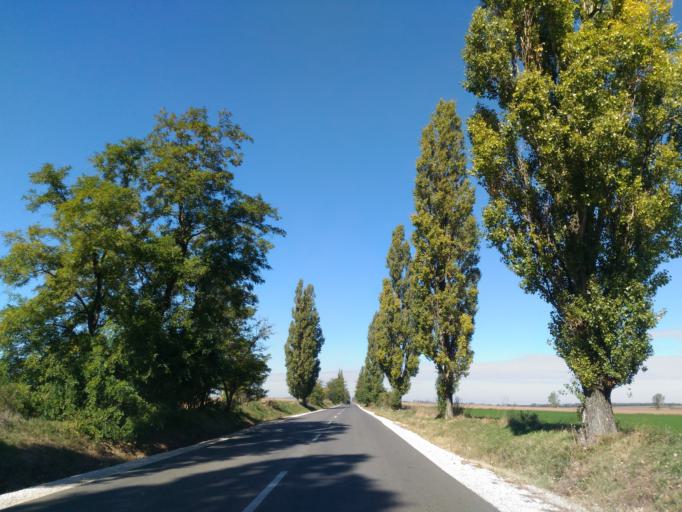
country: HU
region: Fejer
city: Pusztaszabolcs
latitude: 47.1792
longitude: 18.7183
